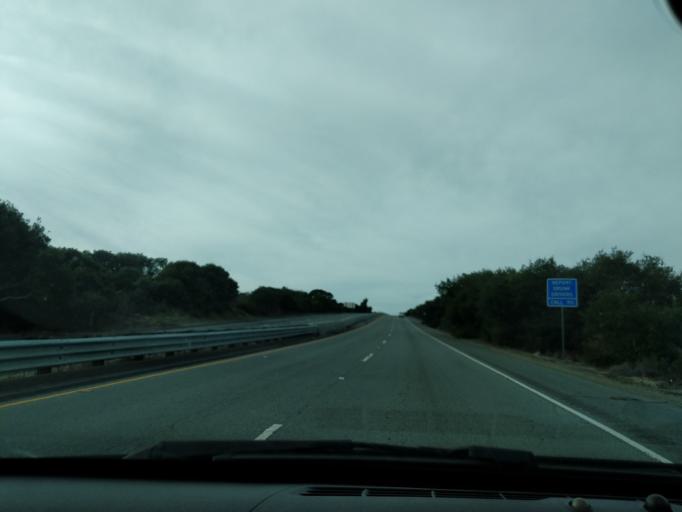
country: US
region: California
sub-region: Santa Barbara County
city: Vandenberg Village
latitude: 34.7043
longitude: -120.4765
